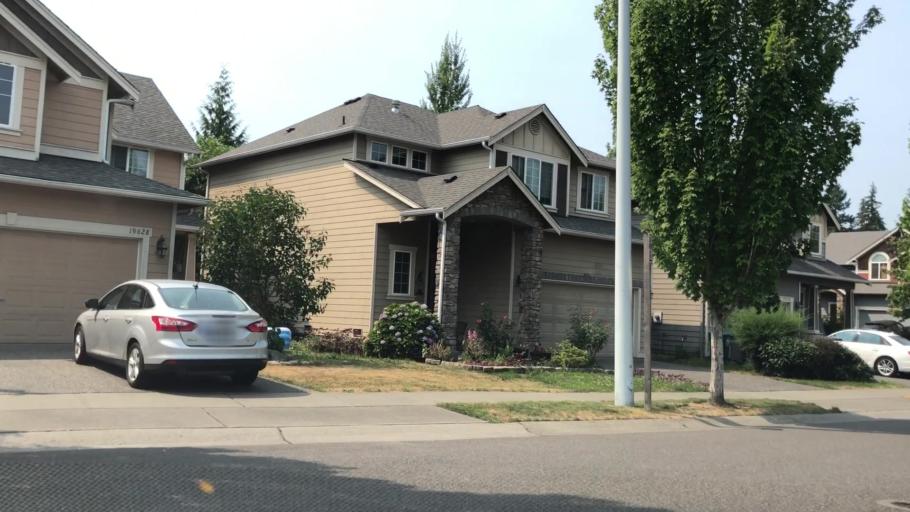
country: US
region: Washington
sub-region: Snohomish County
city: Martha Lake
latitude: 47.8201
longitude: -122.2355
